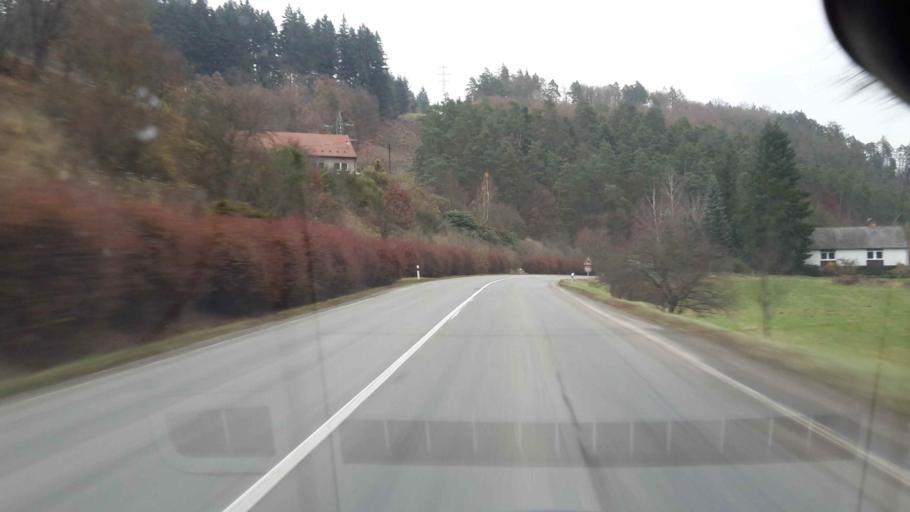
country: CZ
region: South Moravian
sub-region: Okres Blansko
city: Blansko
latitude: 49.3306
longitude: 16.6099
